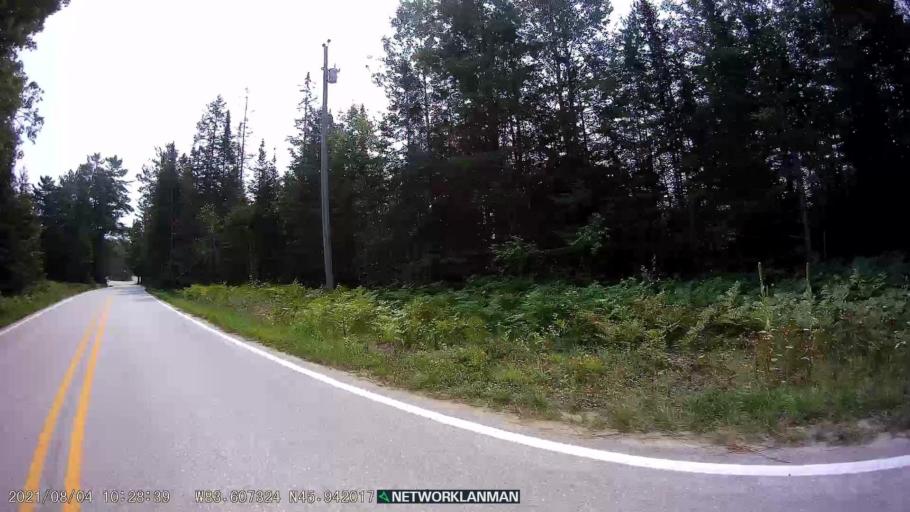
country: CA
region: Ontario
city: Thessalon
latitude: 45.9420
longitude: -83.6072
